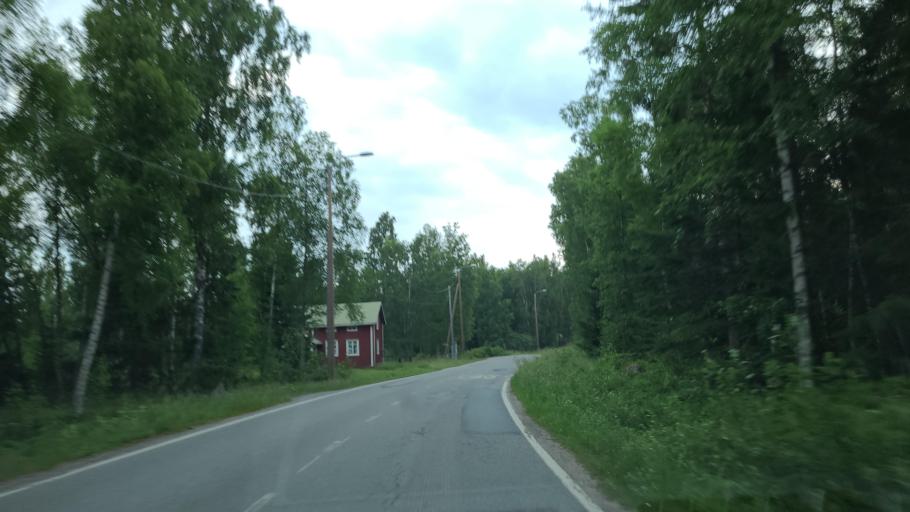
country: FI
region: Ostrobothnia
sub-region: Vaasa
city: Replot
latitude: 63.1775
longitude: 21.2770
